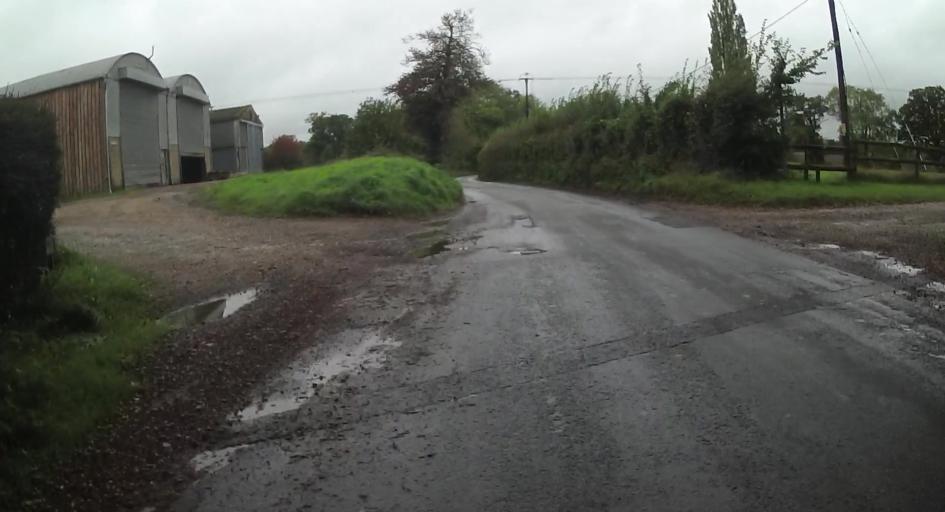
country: GB
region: England
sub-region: Hampshire
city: Tadley
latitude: 51.4115
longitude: -1.1751
